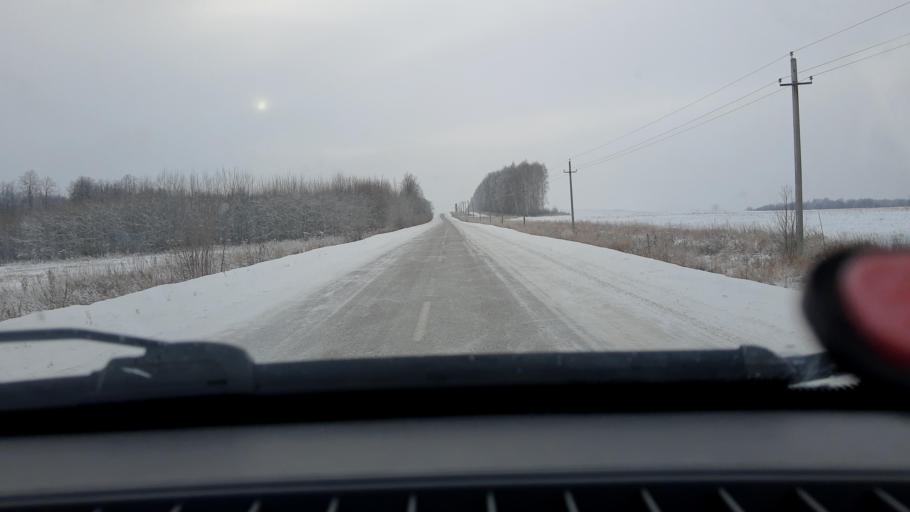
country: RU
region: Bashkortostan
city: Iglino
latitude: 54.6658
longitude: 56.4221
